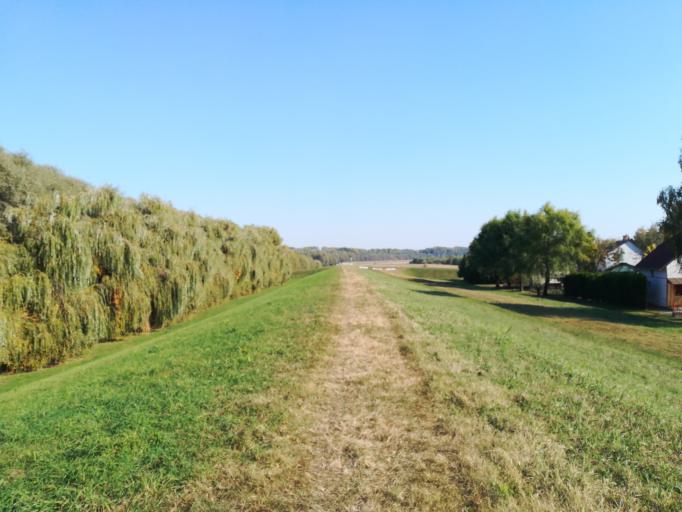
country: HU
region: Bacs-Kiskun
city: Tiszakecske
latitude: 46.9394
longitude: 20.1277
